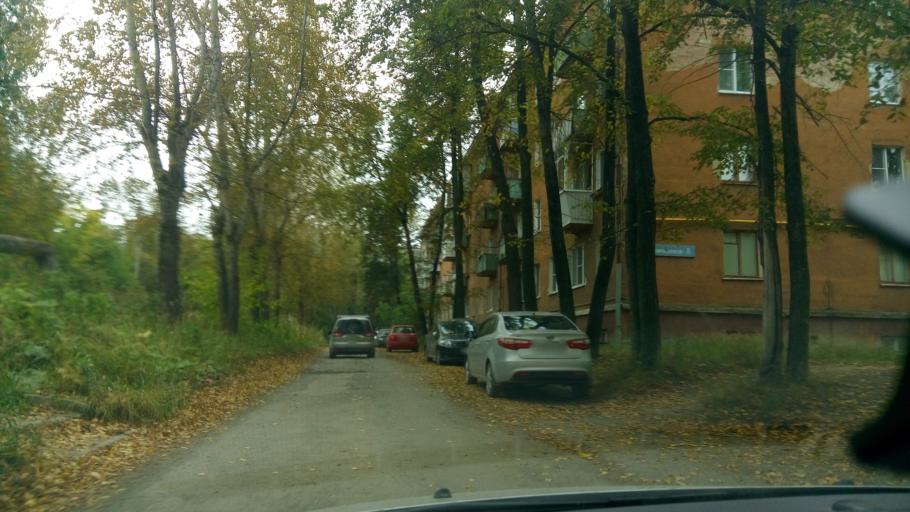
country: RU
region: Sverdlovsk
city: Sovkhoznyy
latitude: 56.7796
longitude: 60.5922
